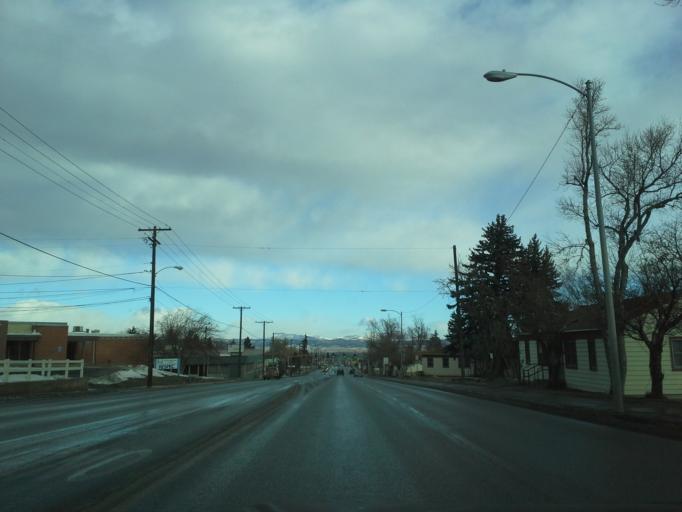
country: US
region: Montana
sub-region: Lewis and Clark County
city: Helena
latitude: 46.5922
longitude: -112.0204
